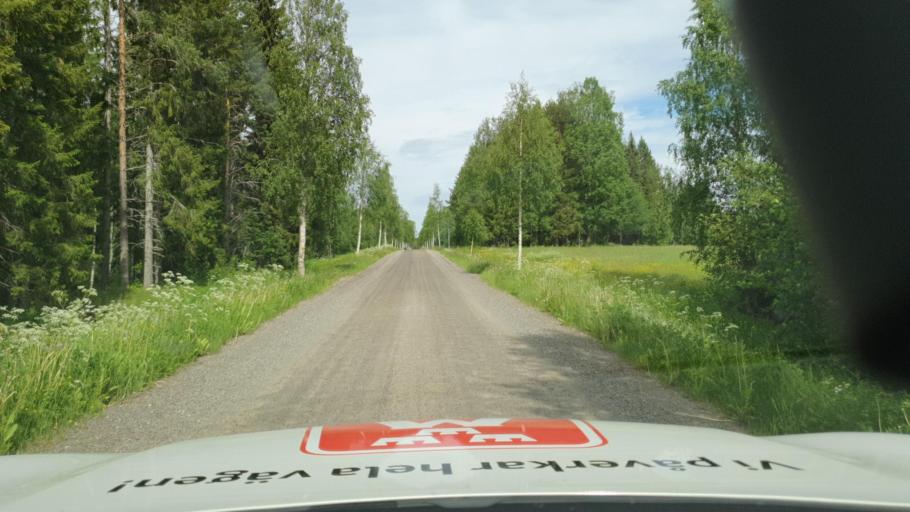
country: SE
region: Vaesterbotten
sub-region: Skelleftea Kommun
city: Burtraesk
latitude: 64.4656
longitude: 20.4674
